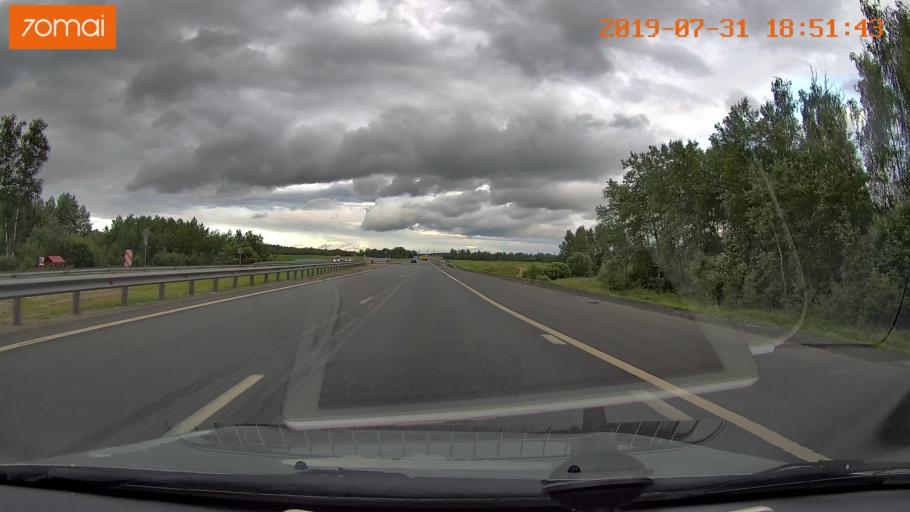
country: RU
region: Moskovskaya
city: Voskresensk
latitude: 55.2196
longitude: 38.6142
